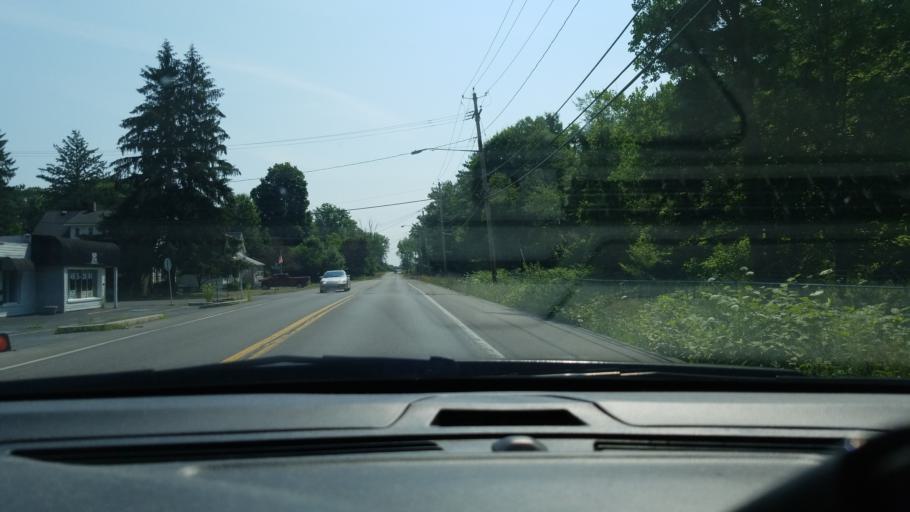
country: US
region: New York
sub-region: Onondaga County
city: Mattydale
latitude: 43.0985
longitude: -76.1284
